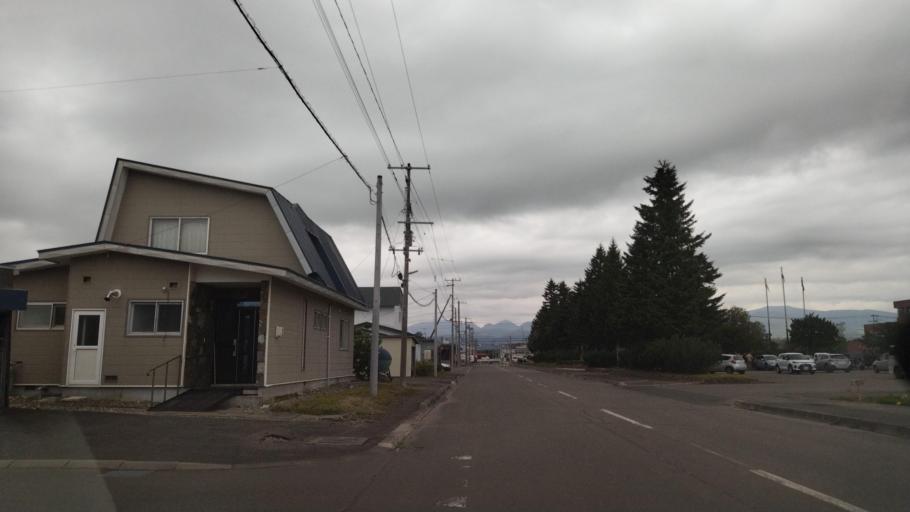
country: JP
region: Hokkaido
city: Otofuke
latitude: 43.2317
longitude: 143.2973
